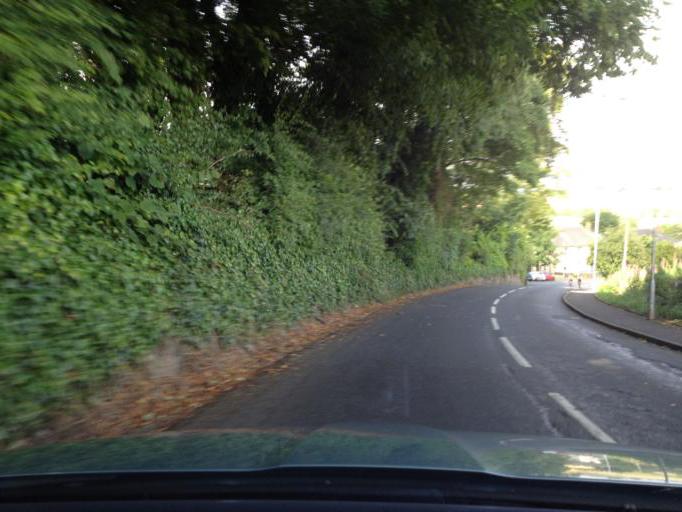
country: GB
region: Scotland
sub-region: North Lanarkshire
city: Harthill
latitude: 55.9306
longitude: -3.7445
